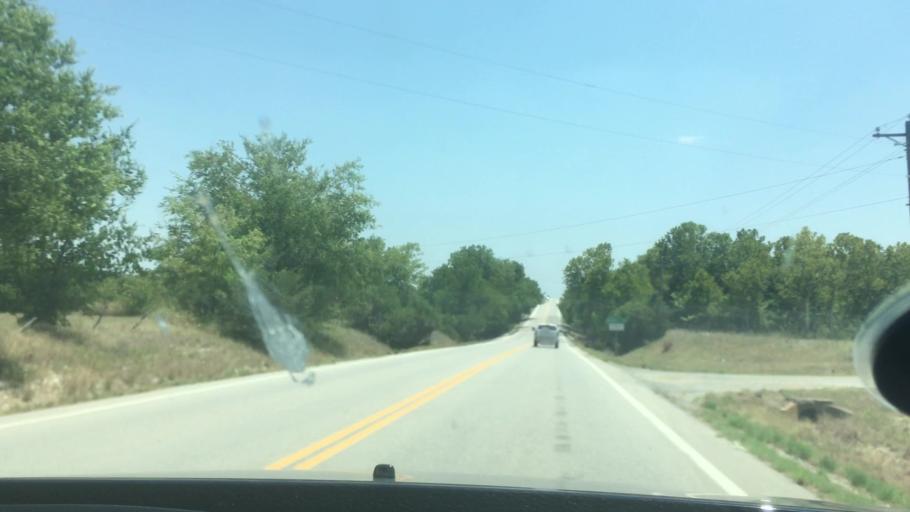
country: US
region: Oklahoma
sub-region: Bryan County
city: Durant
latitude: 34.1575
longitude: -96.3892
